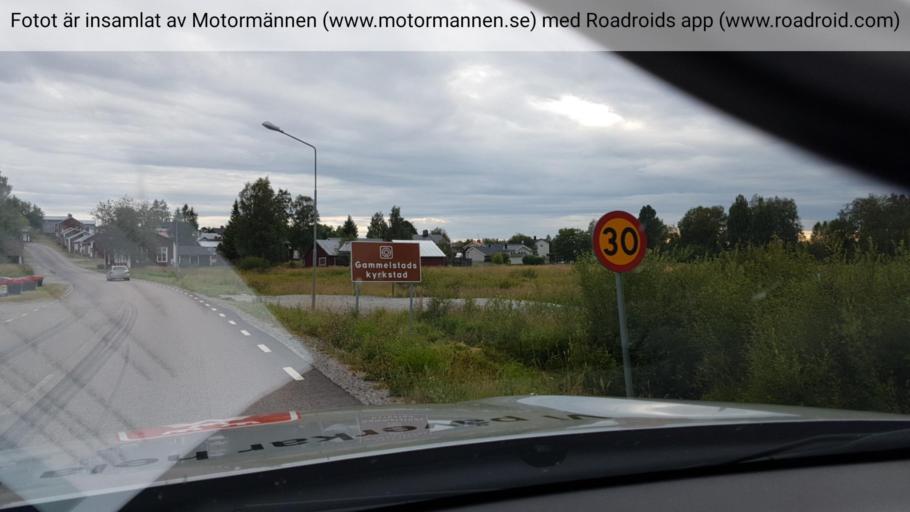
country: SE
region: Norrbotten
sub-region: Lulea Kommun
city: Gammelstad
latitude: 65.6486
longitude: 22.0289
